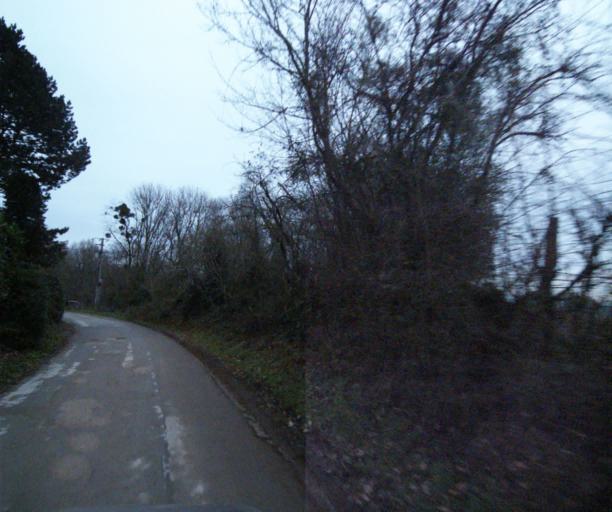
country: FR
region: Ile-de-France
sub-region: Departement de Seine-et-Marne
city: Longperrier
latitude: 49.0599
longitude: 2.6632
